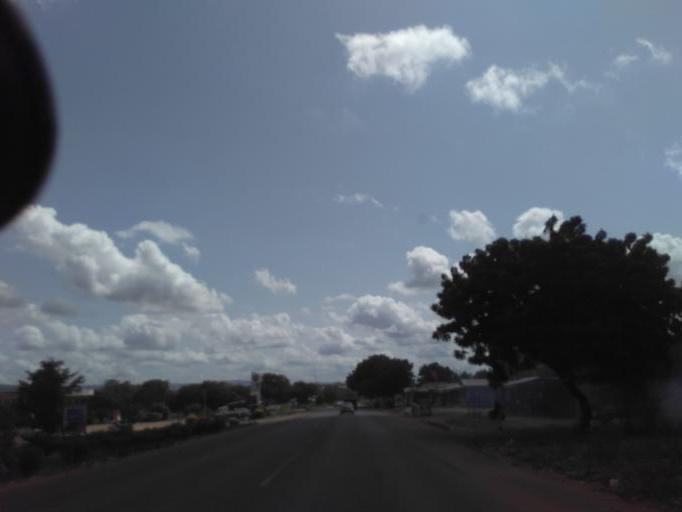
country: GH
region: Eastern
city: Aburi
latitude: 5.7811
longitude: -0.1347
